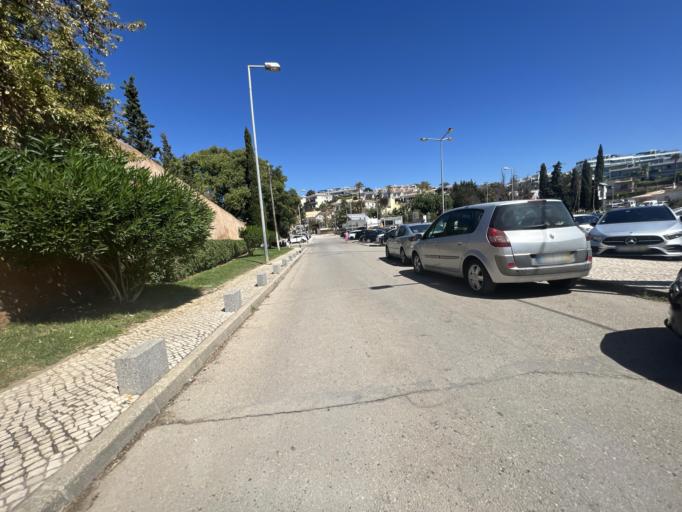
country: PT
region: Faro
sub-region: Portimao
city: Portimao
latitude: 37.1196
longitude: -8.5205
